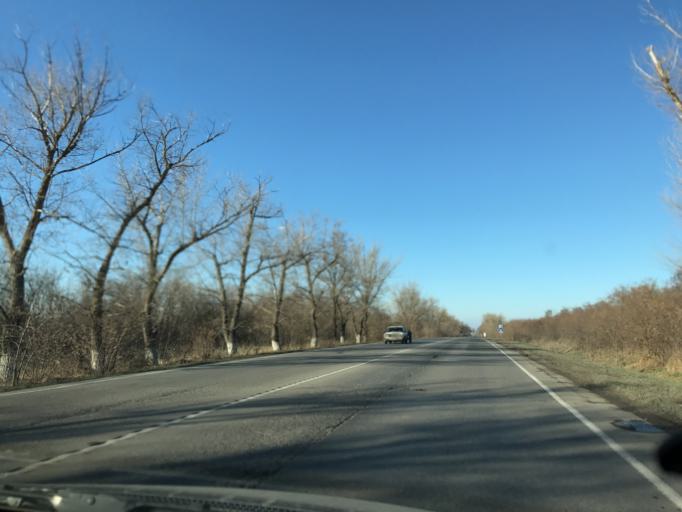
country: RU
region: Rostov
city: Kirovskaya
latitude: 47.0223
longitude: 39.8959
